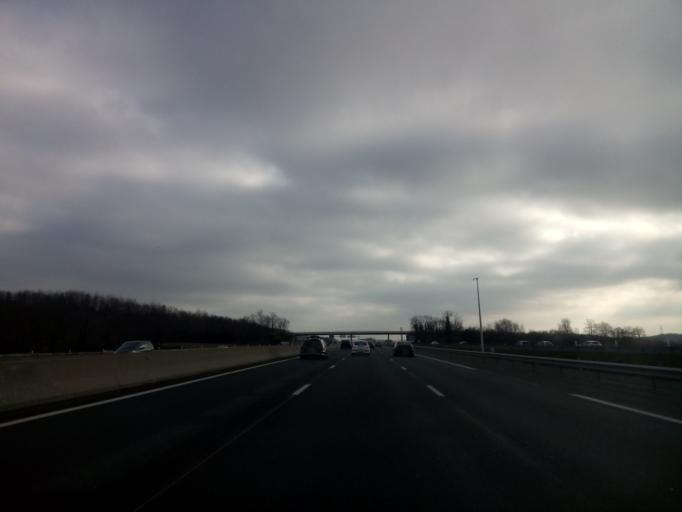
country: FR
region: Rhone-Alpes
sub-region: Departement du Rhone
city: Saint-Laurent-de-Mure
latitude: 45.6692
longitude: 5.0495
